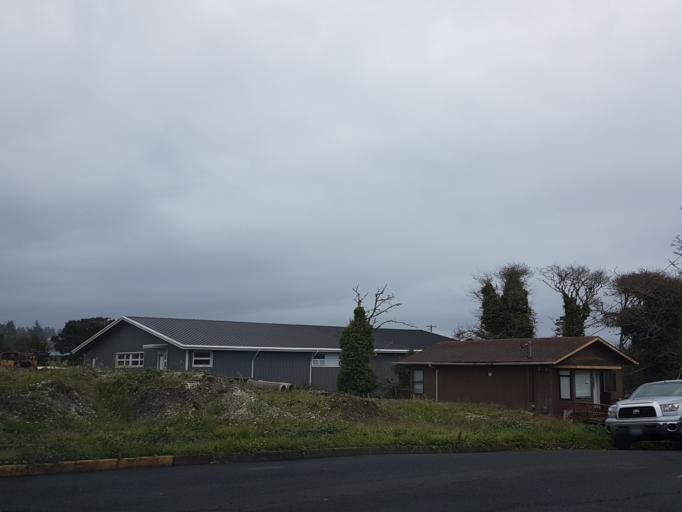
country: US
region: Oregon
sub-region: Lincoln County
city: Newport
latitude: 44.6446
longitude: -124.0557
